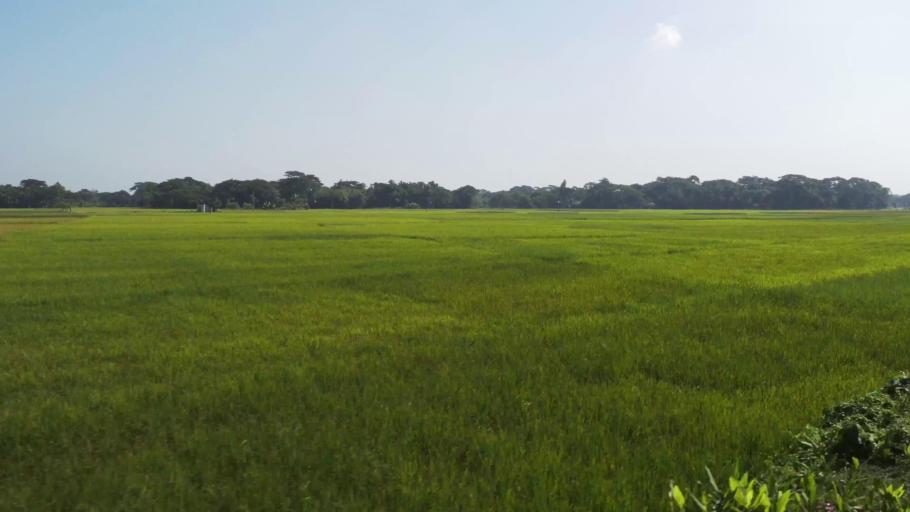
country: BD
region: Dhaka
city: Gafargaon
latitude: 24.5179
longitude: 90.5103
